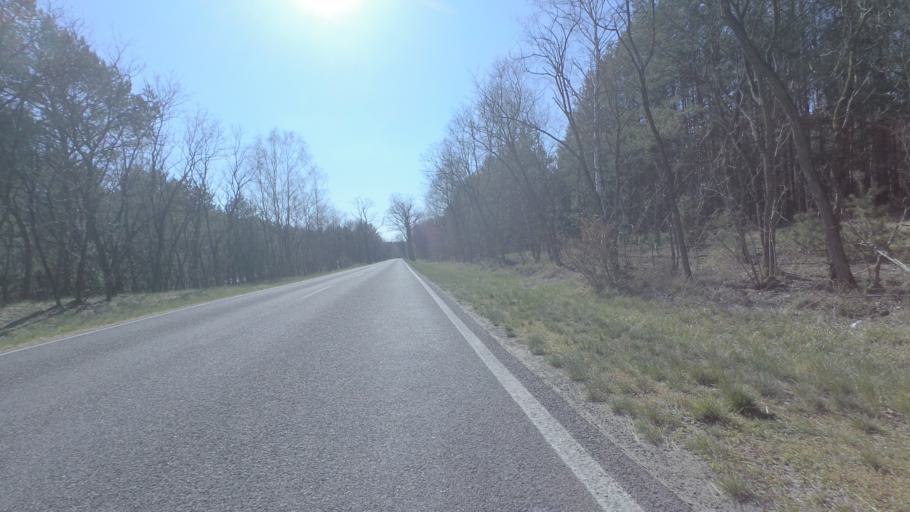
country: DE
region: Brandenburg
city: Munchehofe
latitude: 52.1288
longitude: 13.8150
